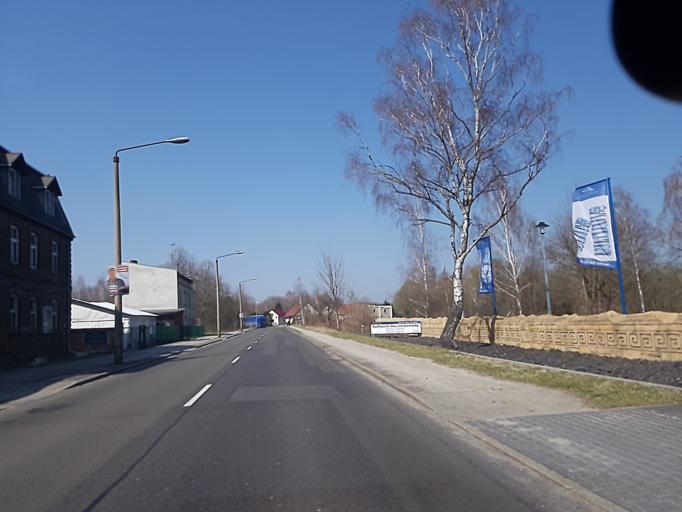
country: DE
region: Brandenburg
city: Tschernitz
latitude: 51.6234
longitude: 14.5889
